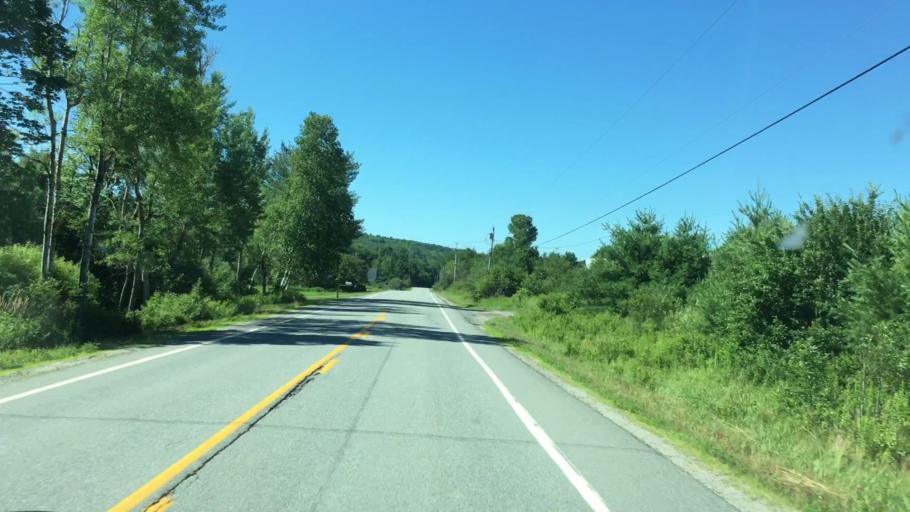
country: US
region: Maine
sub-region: Hancock County
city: Dedham
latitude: 44.6732
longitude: -68.6722
